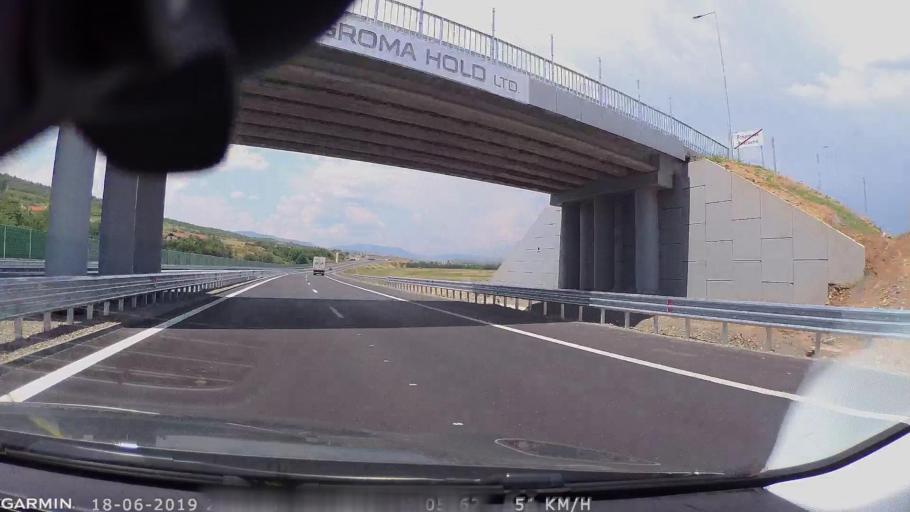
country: BG
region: Blagoevgrad
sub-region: Obshtina Blagoevgrad
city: Blagoevgrad
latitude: 41.9769
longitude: 23.0703
